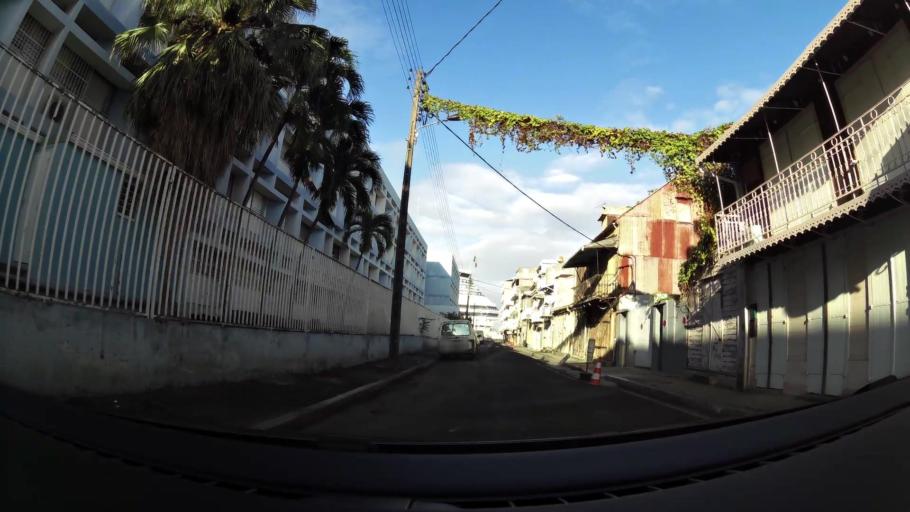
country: GP
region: Guadeloupe
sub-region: Guadeloupe
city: Pointe-a-Pitre
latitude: 16.2390
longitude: -61.5372
